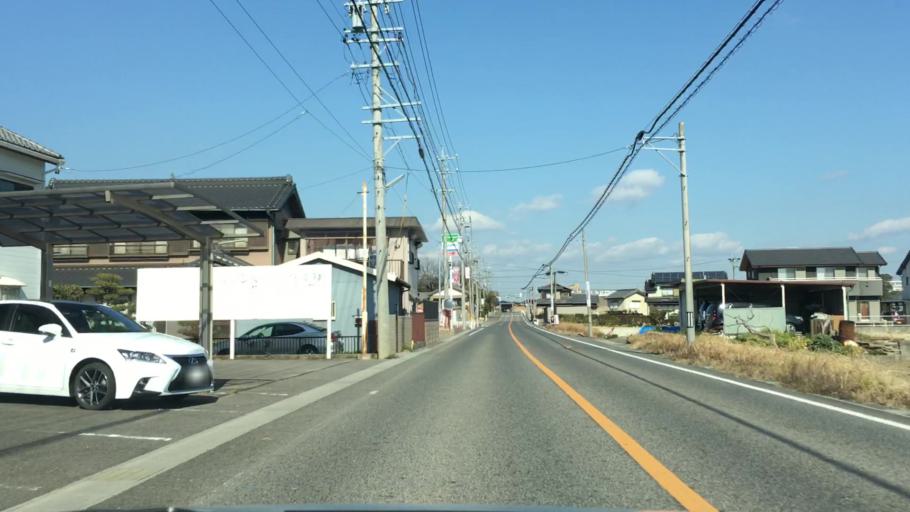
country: JP
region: Aichi
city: Anjo
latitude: 35.0044
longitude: 137.1184
